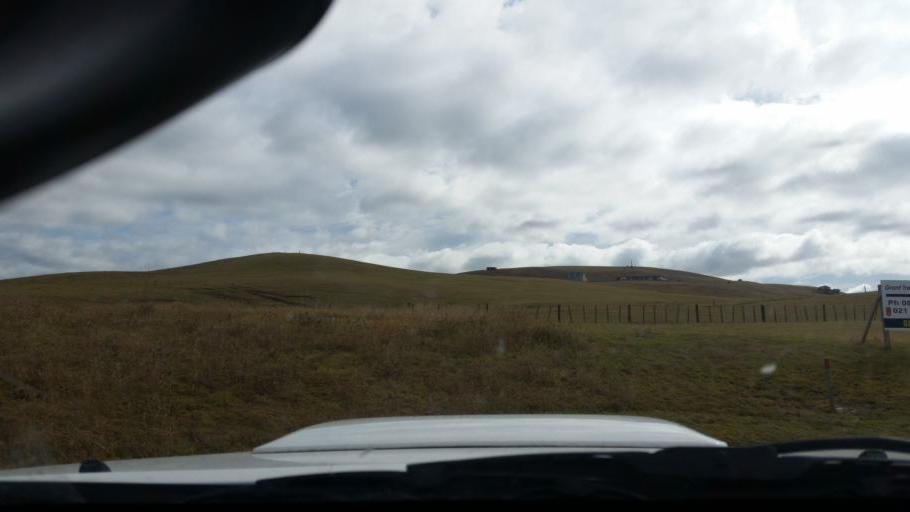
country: NZ
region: Northland
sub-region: Kaipara District
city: Dargaville
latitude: -35.9477
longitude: 173.7457
